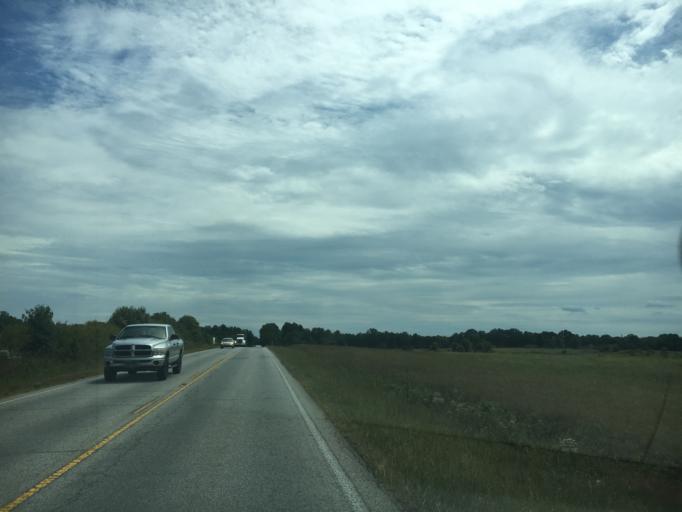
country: US
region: South Carolina
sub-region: Laurens County
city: Laurens
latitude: 34.5505
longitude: -82.0734
